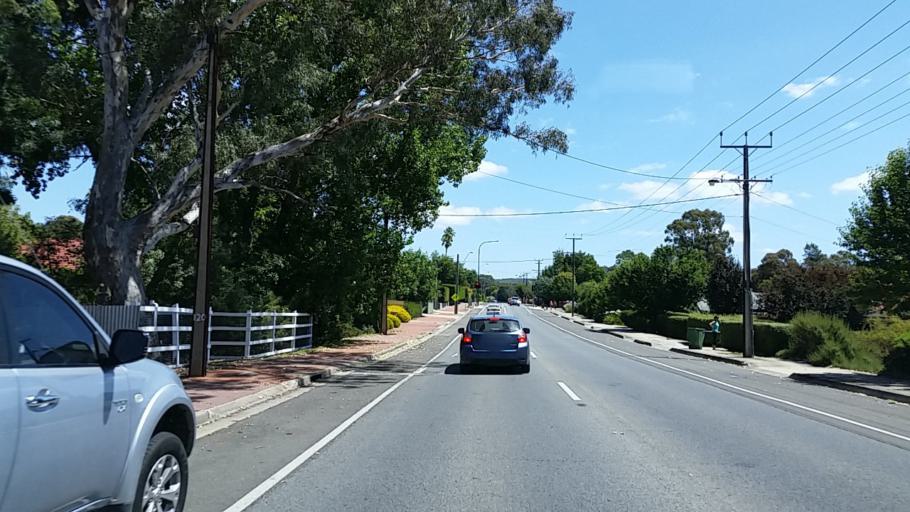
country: AU
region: South Australia
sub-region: Mount Barker
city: Mount Barker
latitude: -35.0472
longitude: 138.8696
